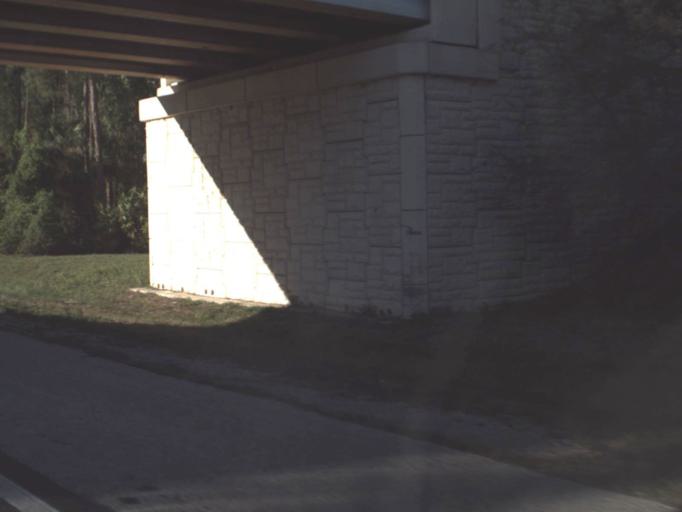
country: US
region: Florida
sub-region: Flagler County
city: Palm Coast
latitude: 29.6459
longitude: -81.2731
